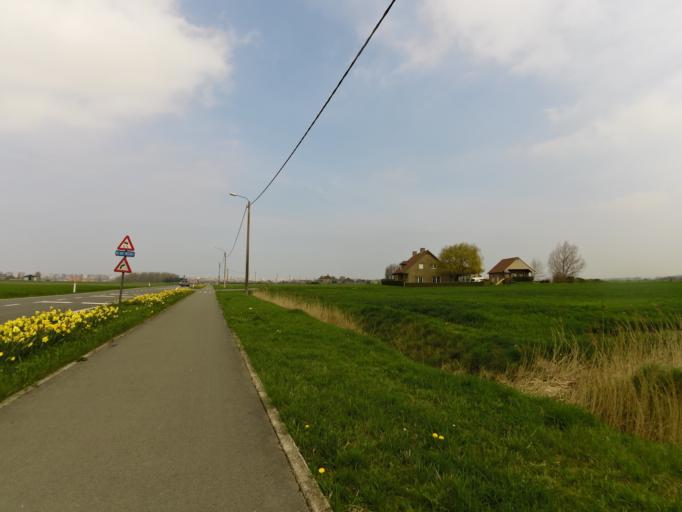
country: BE
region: Flanders
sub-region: Provincie West-Vlaanderen
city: Middelkerke
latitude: 51.1677
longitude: 2.8290
